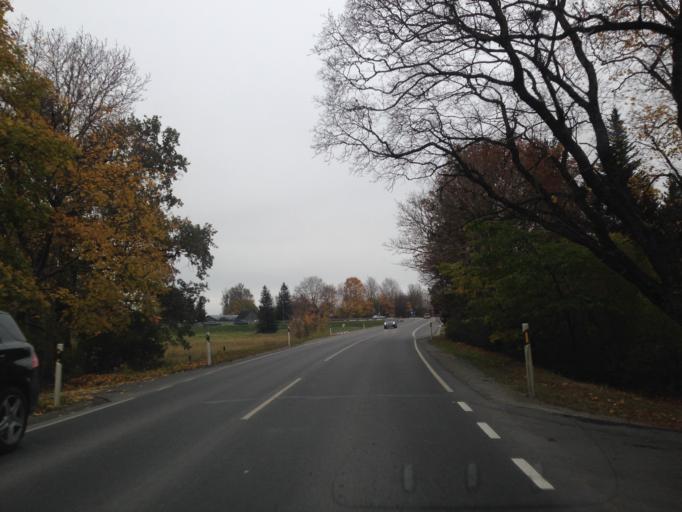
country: EE
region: Harju
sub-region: Harku vald
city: Tabasalu
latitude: 59.3912
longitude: 24.5566
